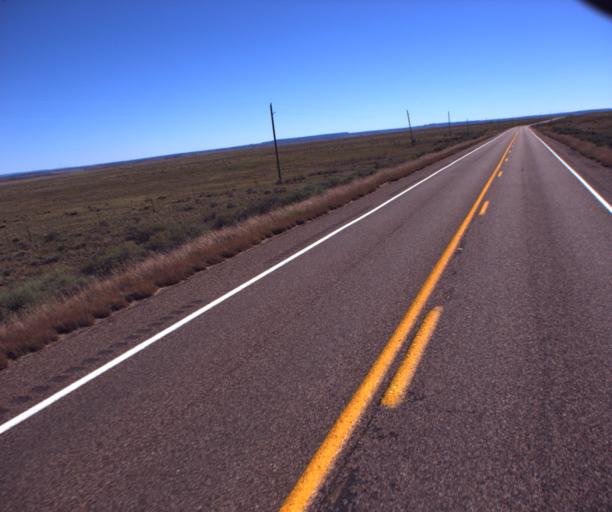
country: US
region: Arizona
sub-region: Apache County
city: Saint Johns
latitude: 34.5399
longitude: -109.4706
